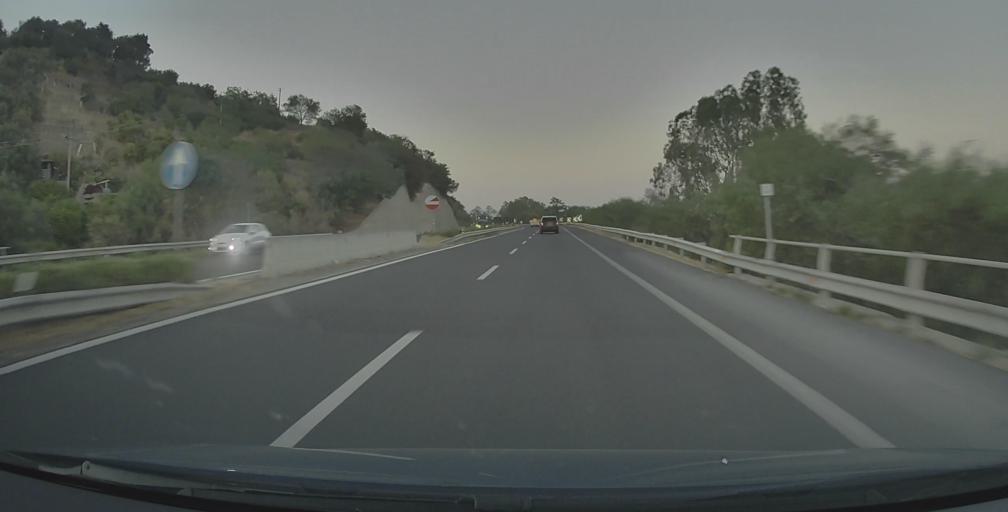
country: IT
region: Sicily
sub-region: Messina
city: Ali Terme
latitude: 38.0009
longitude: 15.4162
